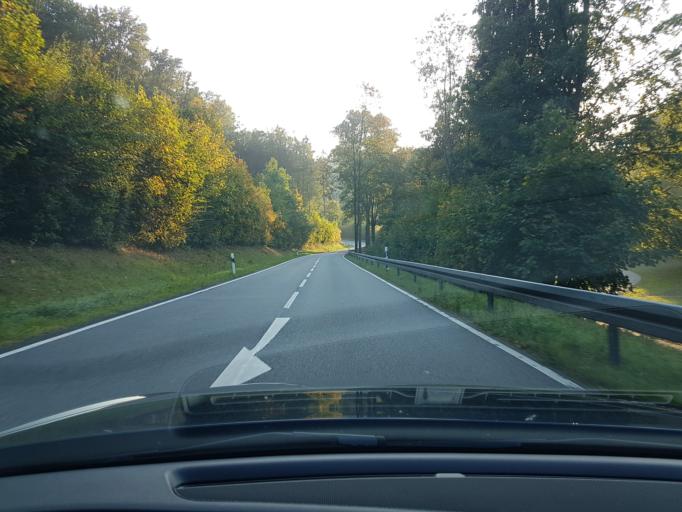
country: DE
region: Hesse
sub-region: Regierungsbezirk Darmstadt
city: Beerfelden
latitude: 49.5462
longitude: 8.9720
